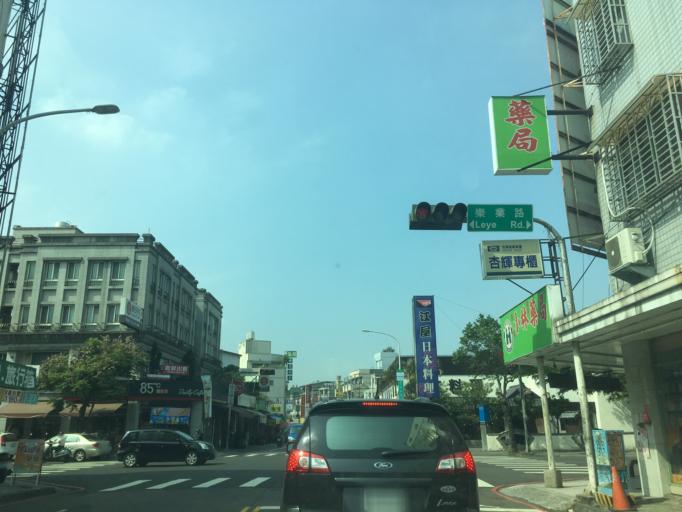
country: TW
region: Taiwan
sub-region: Taichung City
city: Taichung
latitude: 24.1371
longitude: 120.7065
